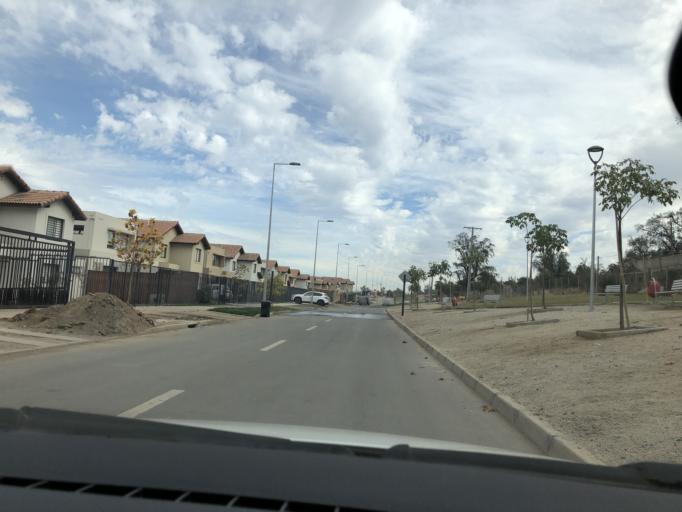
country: CL
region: Santiago Metropolitan
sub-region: Provincia de Cordillera
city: Puente Alto
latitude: -33.5802
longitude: -70.5089
